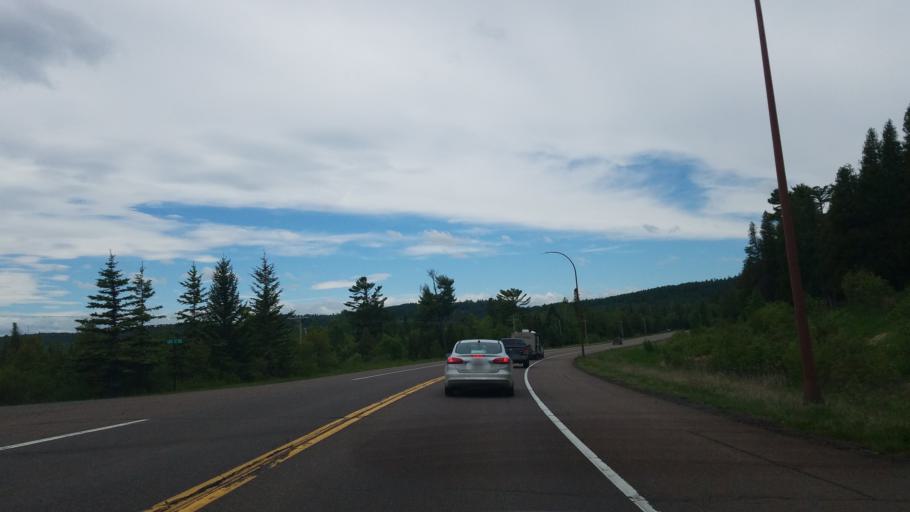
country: US
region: Minnesota
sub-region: Lake County
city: Two Harbors
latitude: 47.0959
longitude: -91.5511
